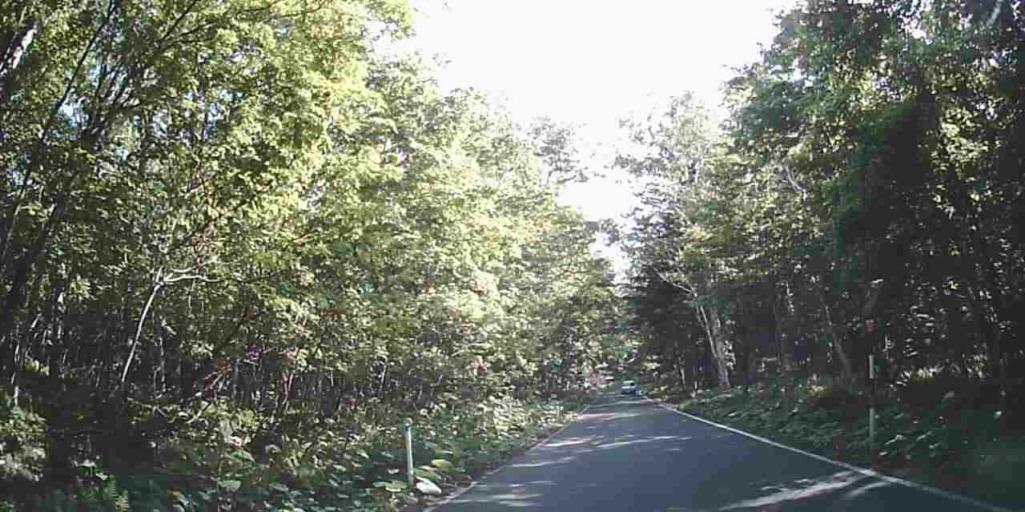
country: JP
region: Hokkaido
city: Shiraoi
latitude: 42.7216
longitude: 141.4117
